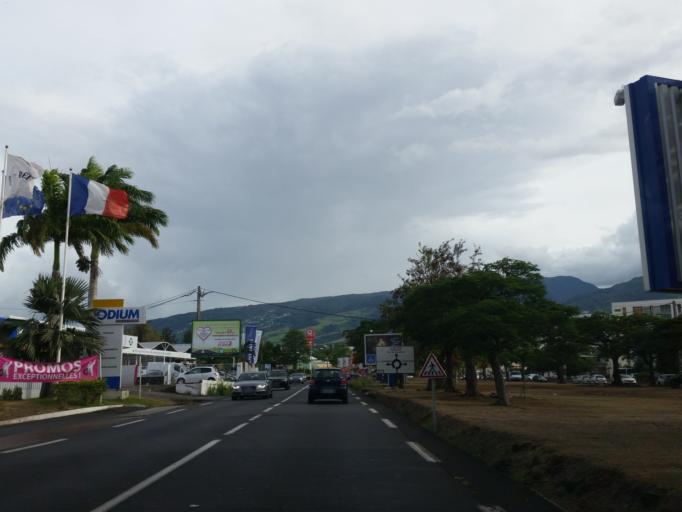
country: RE
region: Reunion
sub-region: Reunion
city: Saint-Denis
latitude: -20.8906
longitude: 55.4907
